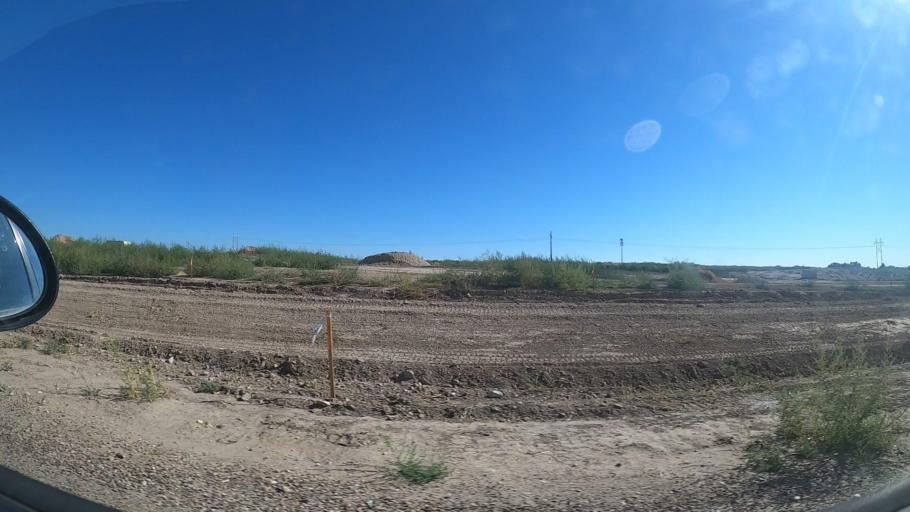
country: US
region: Idaho
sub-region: Canyon County
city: Nampa
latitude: 43.5472
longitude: -116.6114
